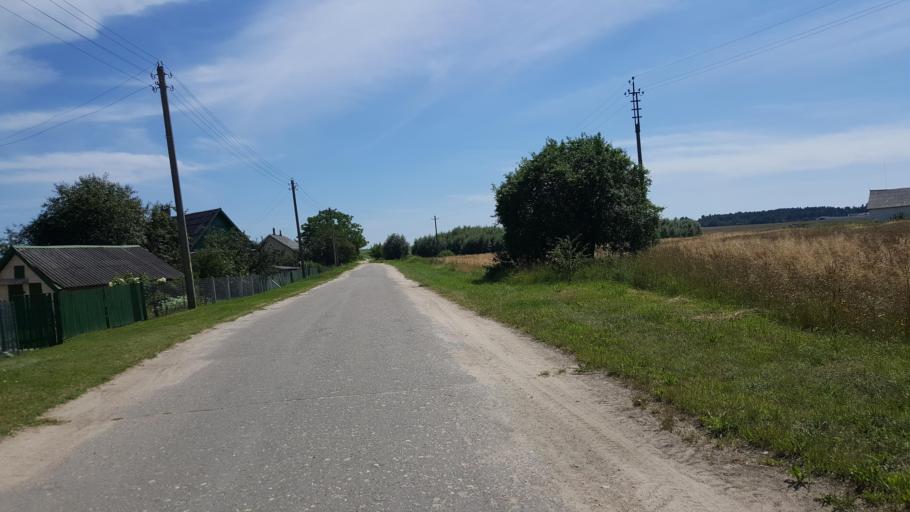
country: BY
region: Brest
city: Pruzhany
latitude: 52.5505
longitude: 24.2194
